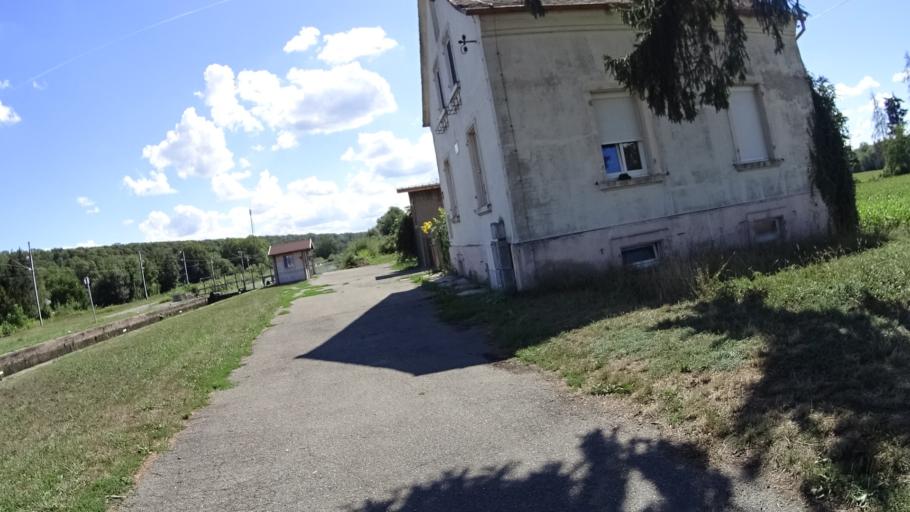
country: FR
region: Alsace
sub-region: Departement du Haut-Rhin
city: Didenheim
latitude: 47.7106
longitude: 7.3112
